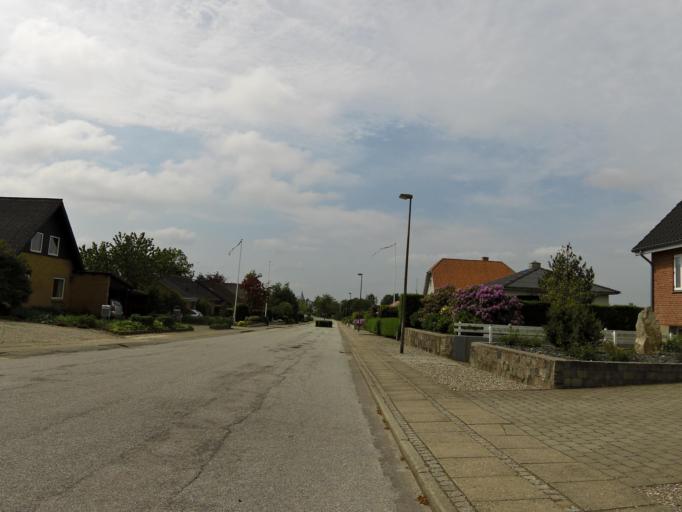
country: DK
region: South Denmark
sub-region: Haderslev Kommune
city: Vojens
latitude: 55.2712
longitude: 9.1830
